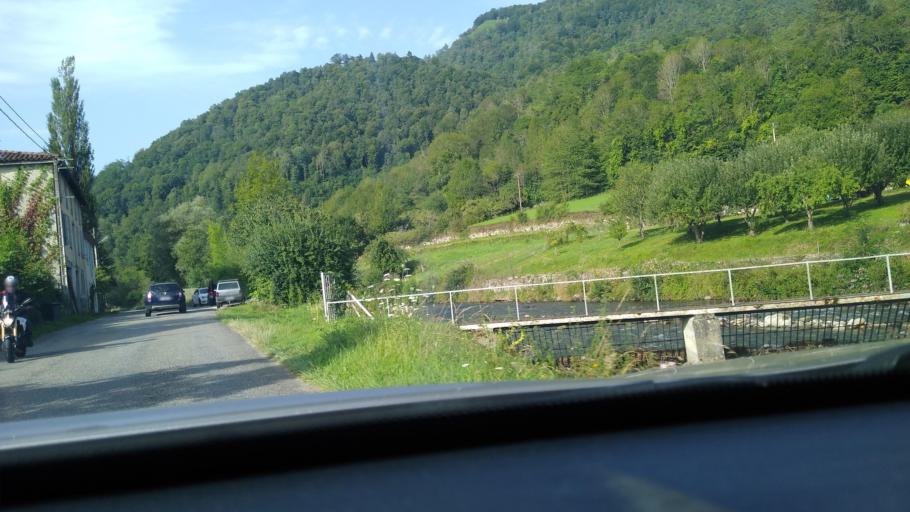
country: FR
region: Midi-Pyrenees
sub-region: Departement de l'Ariege
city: Saint-Girons
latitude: 42.8619
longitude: 1.1998
